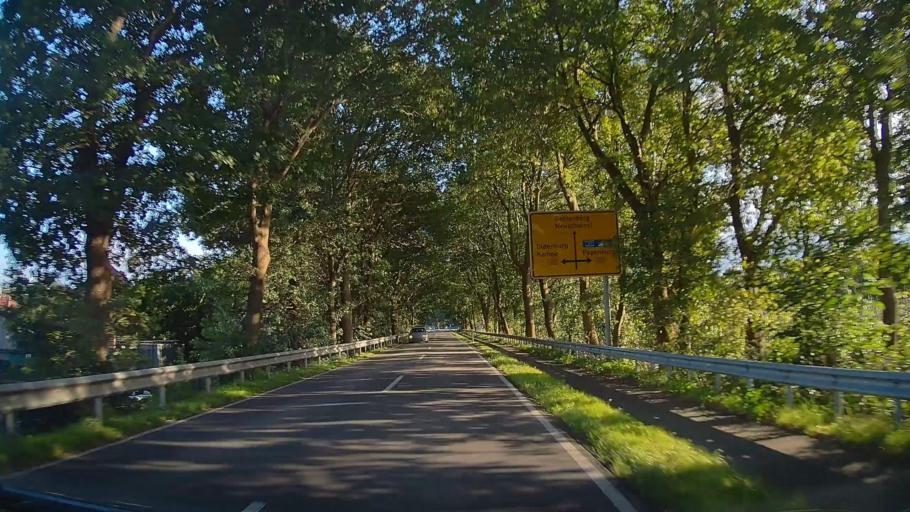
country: DE
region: Lower Saxony
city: Hilkenbrook
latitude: 53.0292
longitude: 7.7465
